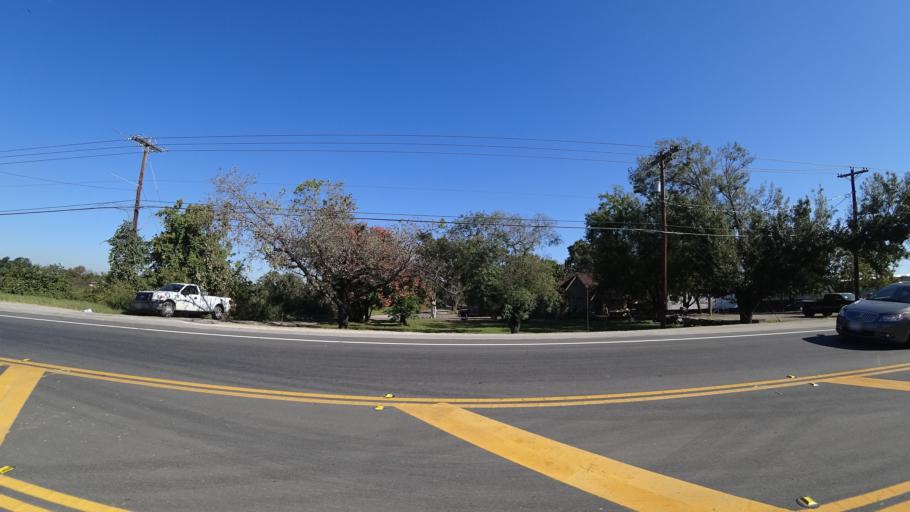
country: US
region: Texas
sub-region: Travis County
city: Hornsby Bend
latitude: 30.2502
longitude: -97.5892
